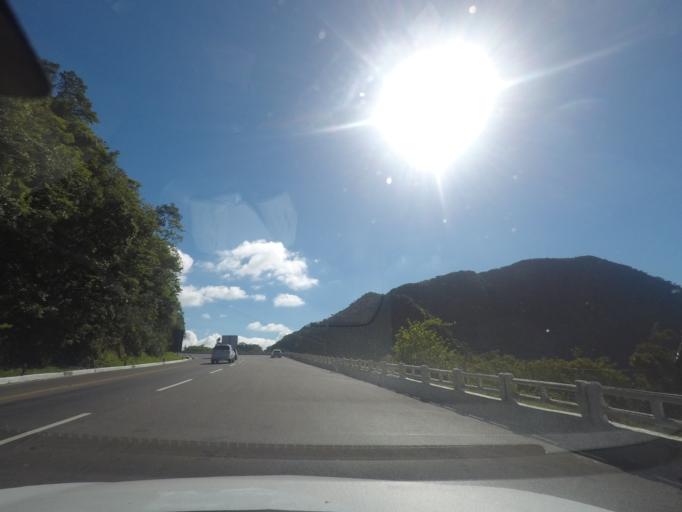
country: BR
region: Rio de Janeiro
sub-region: Teresopolis
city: Teresopolis
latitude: -22.4635
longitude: -42.9891
